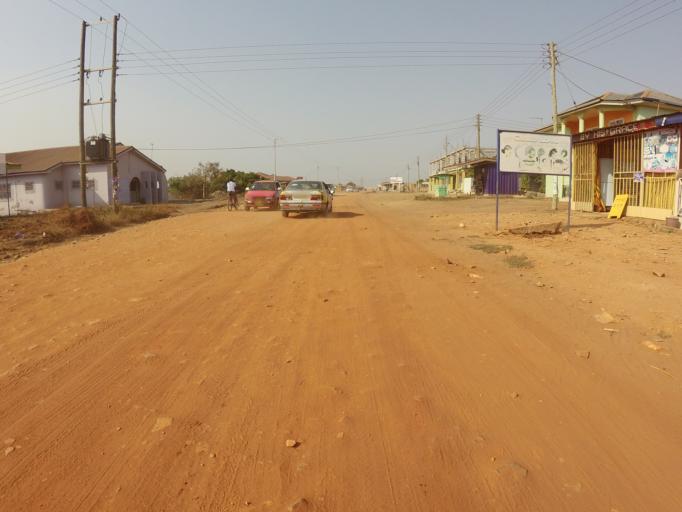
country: GH
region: Greater Accra
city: Tema
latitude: 5.7024
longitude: 0.0575
